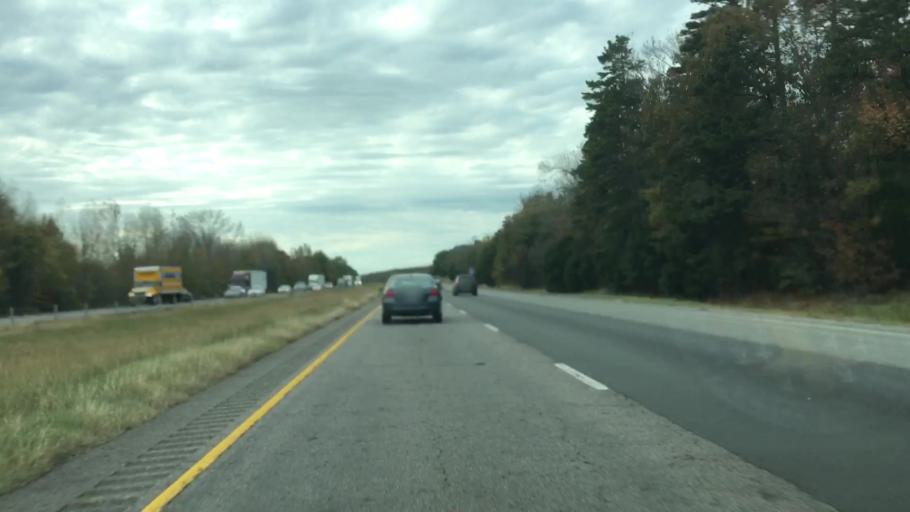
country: US
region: Arkansas
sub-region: Faulkner County
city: Conway
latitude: 35.1548
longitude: -92.5586
